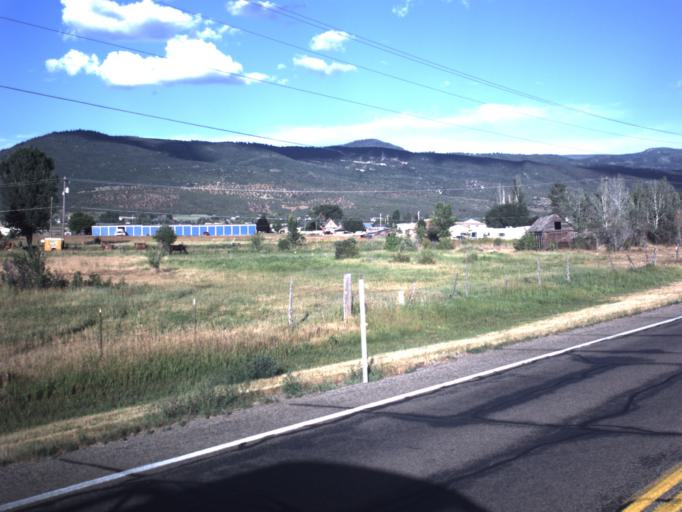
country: US
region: Utah
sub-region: Sanpete County
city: Fairview
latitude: 39.6368
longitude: -111.4447
